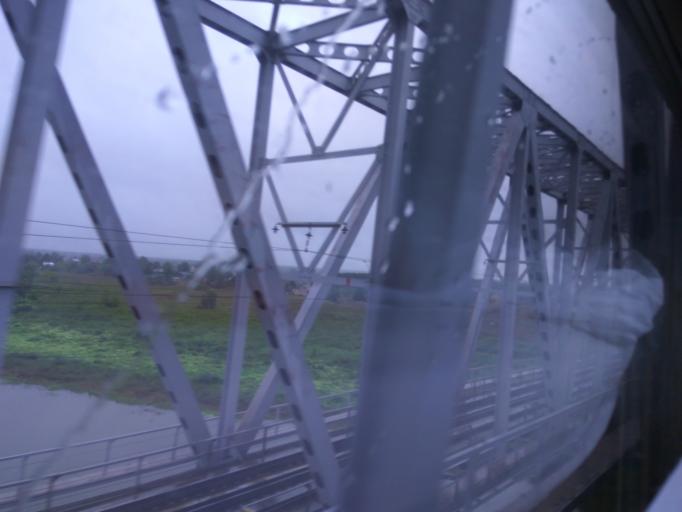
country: RU
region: Moskovskaya
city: Kashira
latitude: 54.8617
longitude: 38.1649
